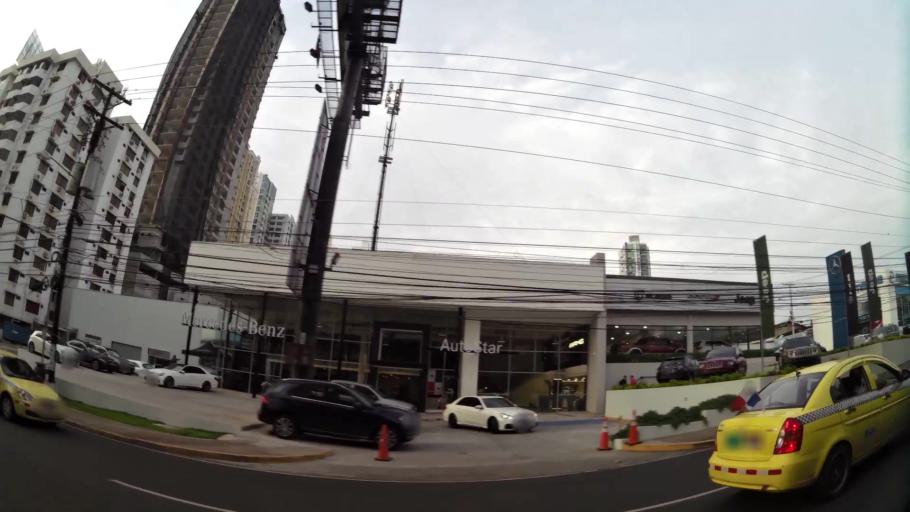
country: PA
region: Panama
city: Panama
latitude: 8.9930
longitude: -79.5045
